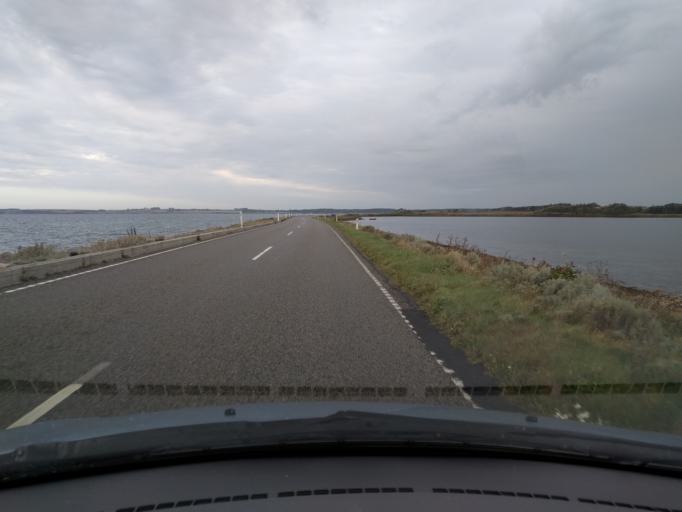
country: DK
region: South Denmark
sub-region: Assens Kommune
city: Assens
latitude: 55.1832
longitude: 9.9850
